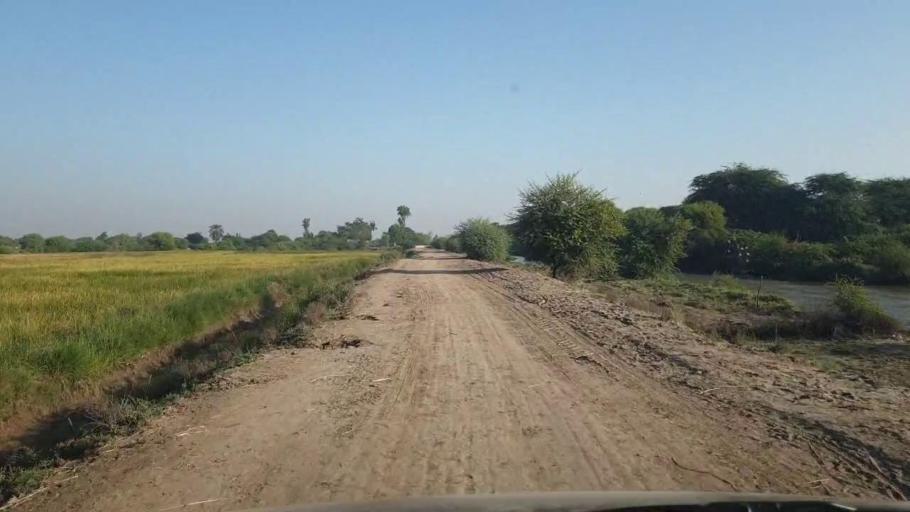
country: PK
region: Sindh
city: Badin
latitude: 24.6861
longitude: 68.8155
